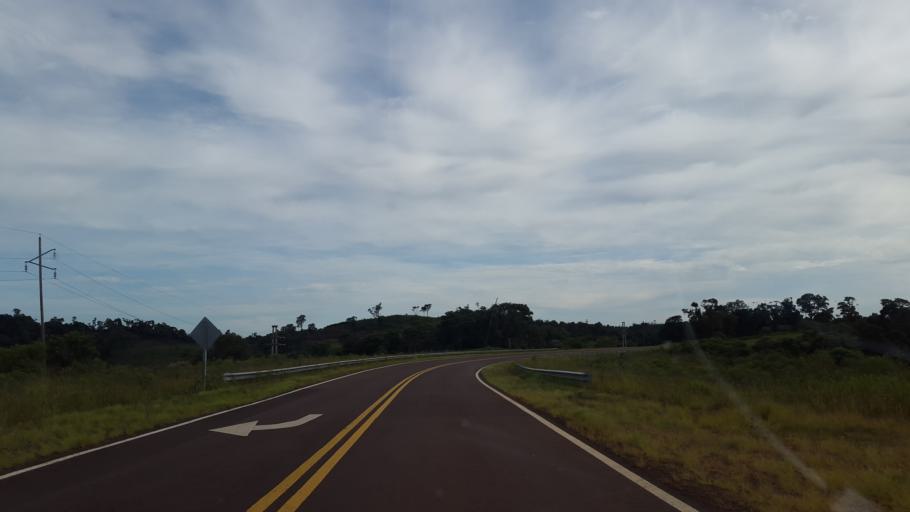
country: AR
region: Misiones
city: Bernardo de Irigoyen
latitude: -26.3944
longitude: -53.8075
